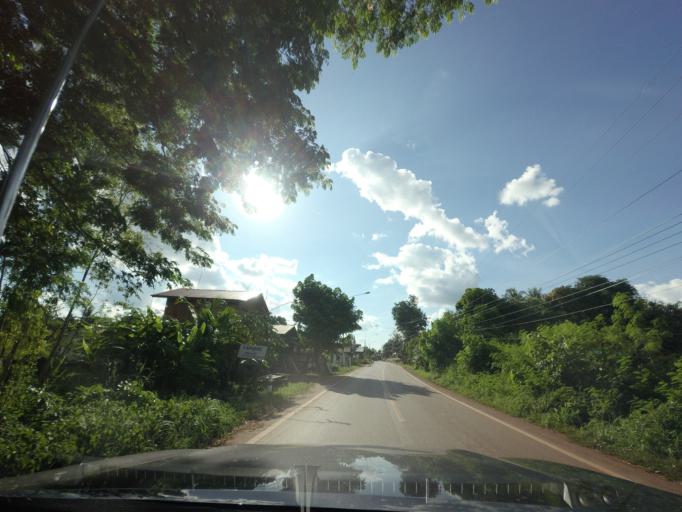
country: TH
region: Changwat Udon Thani
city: Ban Dung
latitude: 17.7461
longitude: 103.3311
